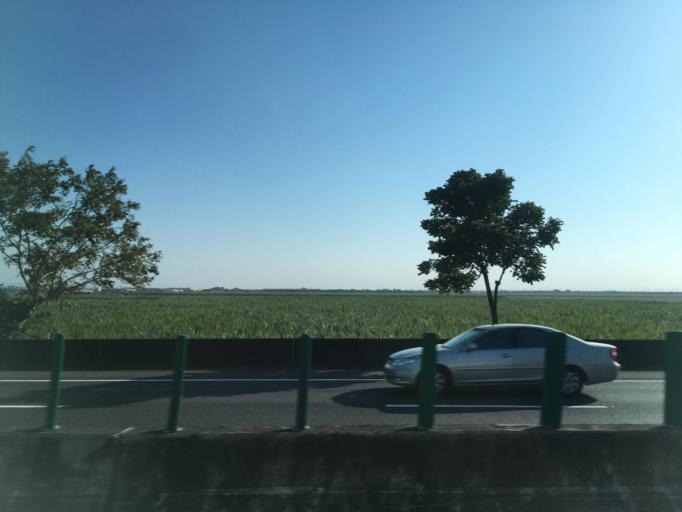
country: TW
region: Taiwan
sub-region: Chiayi
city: Taibao
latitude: 23.4285
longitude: 120.3293
